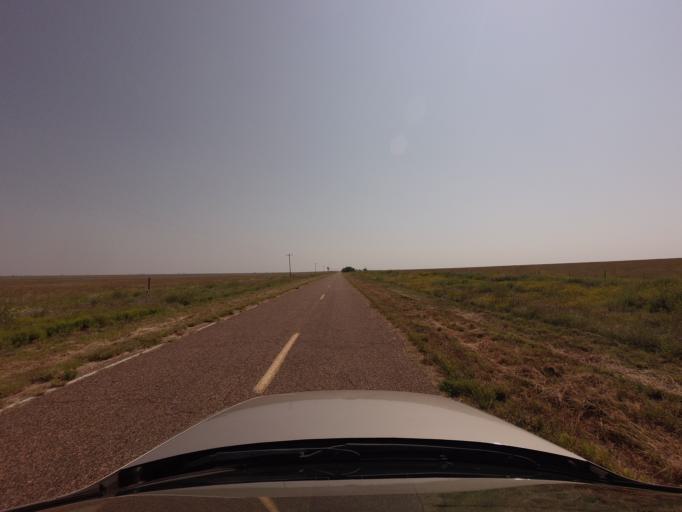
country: US
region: New Mexico
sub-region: Curry County
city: Cannon Air Force Base
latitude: 34.6336
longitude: -103.6318
